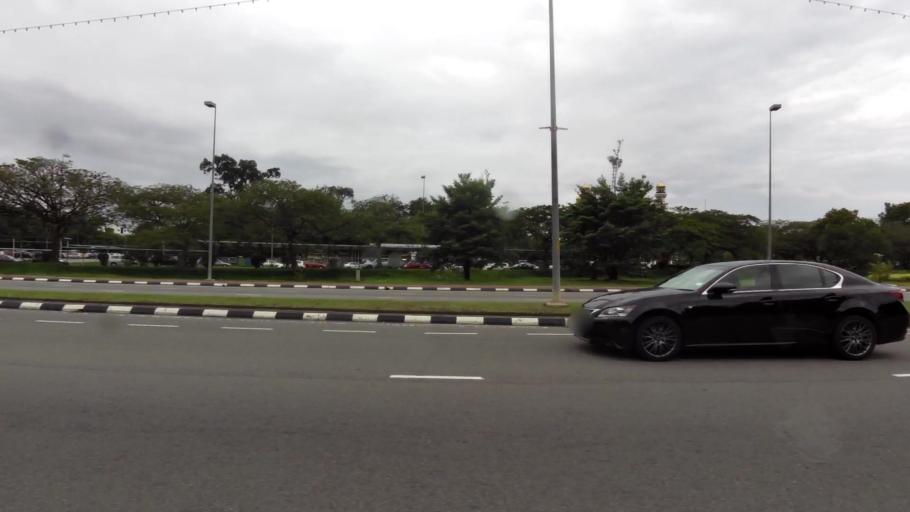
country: BN
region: Brunei and Muara
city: Bandar Seri Begawan
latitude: 4.9010
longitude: 114.9233
